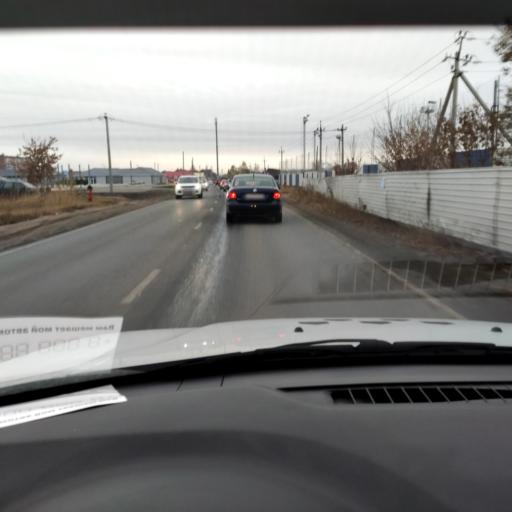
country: RU
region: Samara
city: Tol'yatti
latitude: 53.5123
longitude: 49.2451
